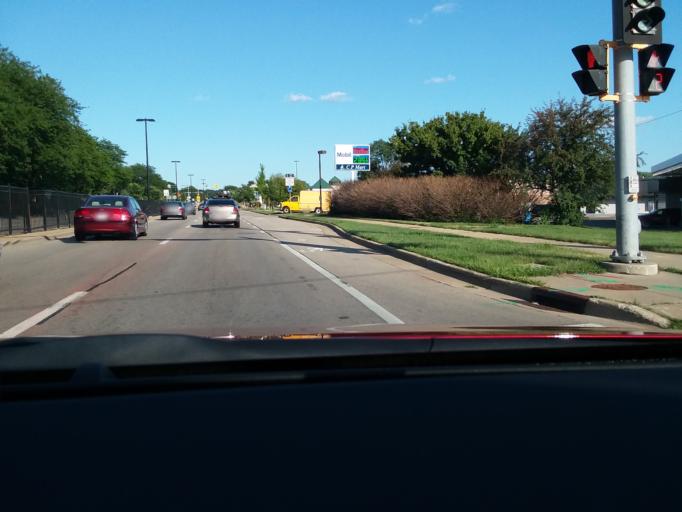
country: US
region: Wisconsin
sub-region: Dane County
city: Maple Bluff
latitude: 43.1306
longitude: -89.3633
